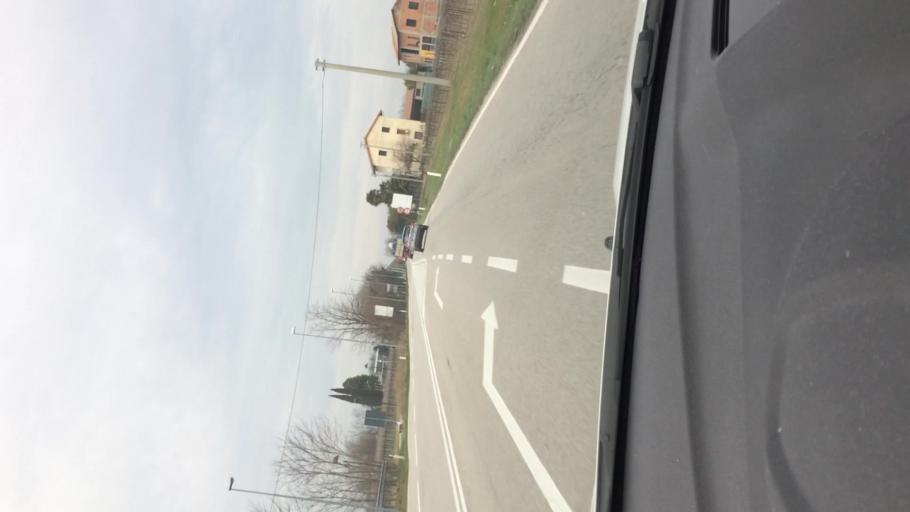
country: IT
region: Friuli Venezia Giulia
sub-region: Provincia di Pordenone
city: Rosa
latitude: 45.9290
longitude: 12.8725
